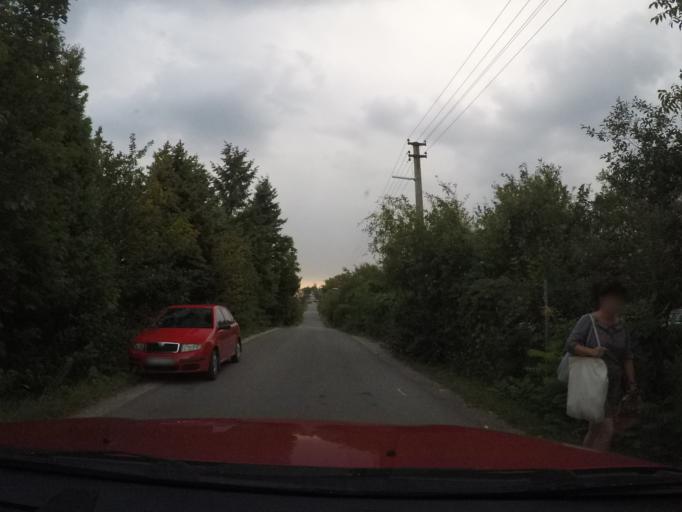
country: SK
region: Kosicky
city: Kosice
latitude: 48.6926
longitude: 21.2092
